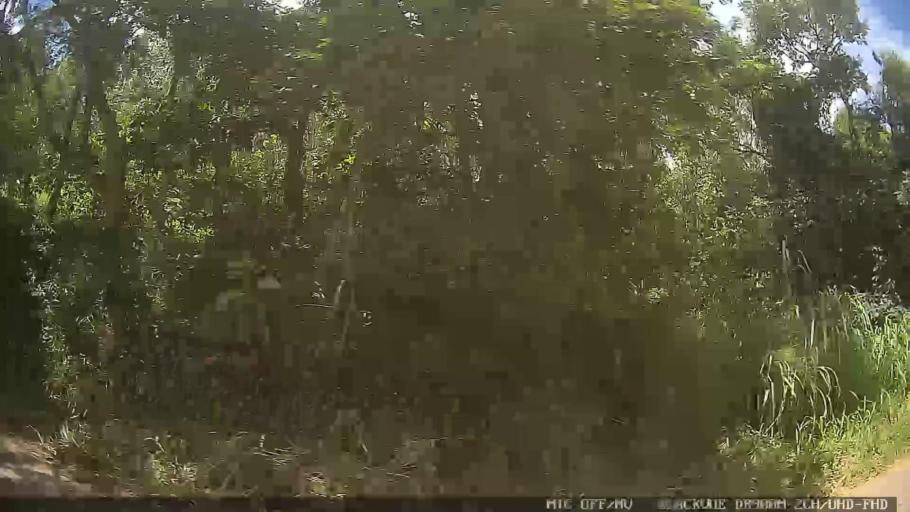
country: BR
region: Minas Gerais
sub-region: Extrema
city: Extrema
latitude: -22.8064
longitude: -46.4628
